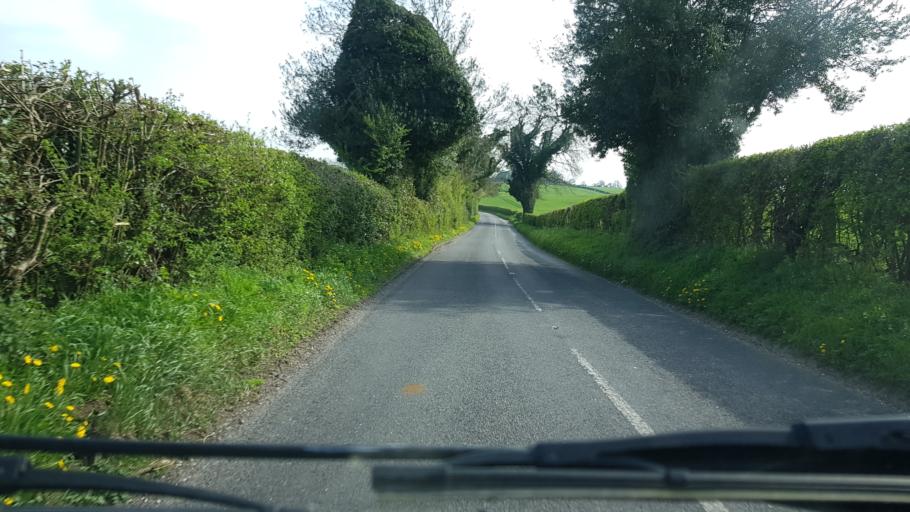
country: GB
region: England
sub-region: Hampshire
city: Overton
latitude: 51.2856
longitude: -1.2622
